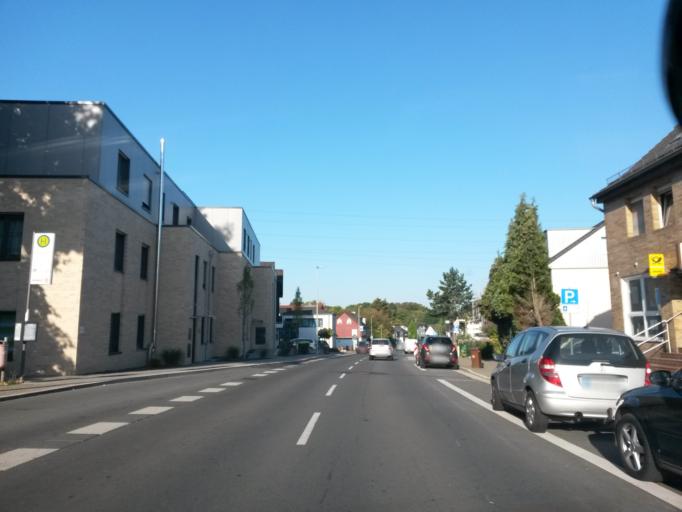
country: DE
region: North Rhine-Westphalia
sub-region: Regierungsbezirk Koln
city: Bergisch Gladbach
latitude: 50.9656
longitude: 7.1827
